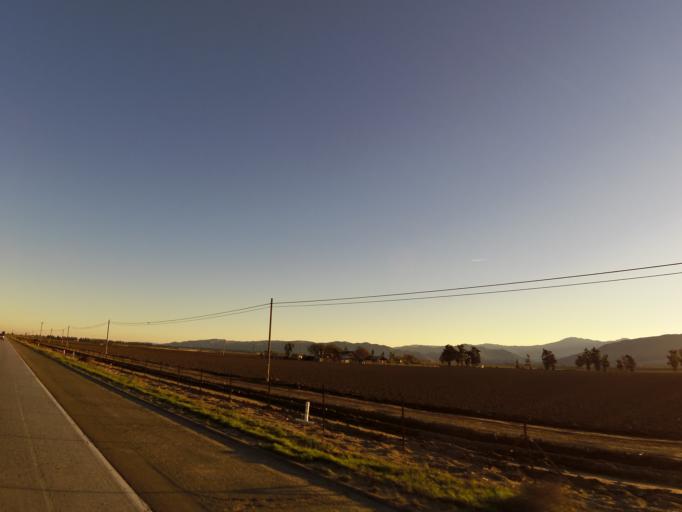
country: US
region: California
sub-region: Monterey County
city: Soledad
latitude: 36.3774
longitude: -121.2940
